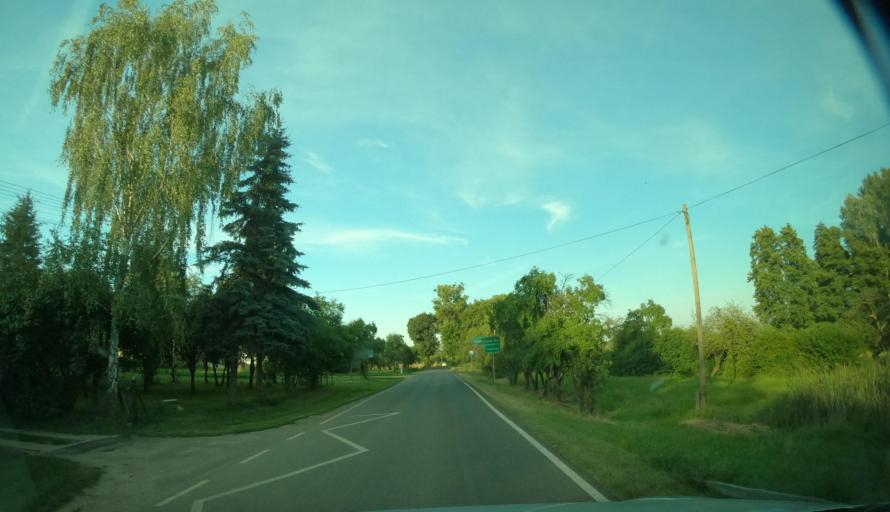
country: PL
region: Kujawsko-Pomorskie
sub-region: Bydgoszcz
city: Fordon
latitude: 53.2282
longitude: 18.2012
